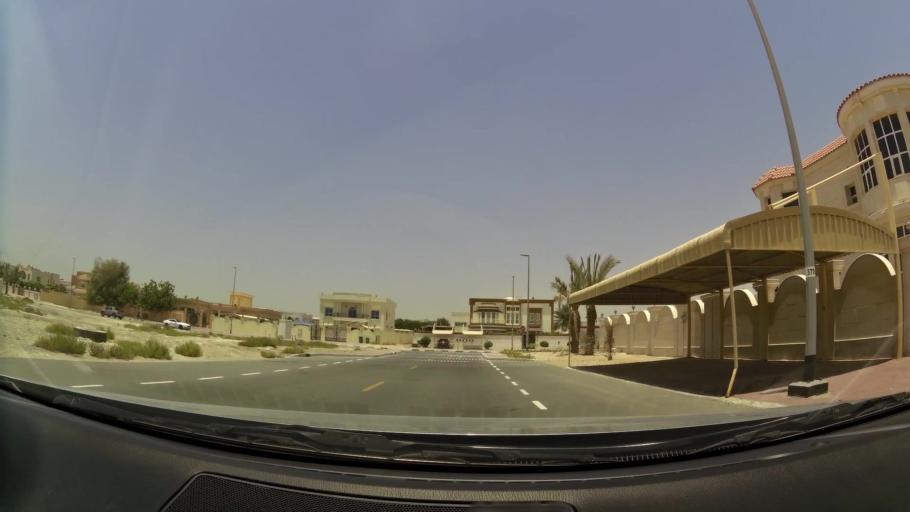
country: AE
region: Dubai
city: Dubai
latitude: 25.0963
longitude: 55.1914
